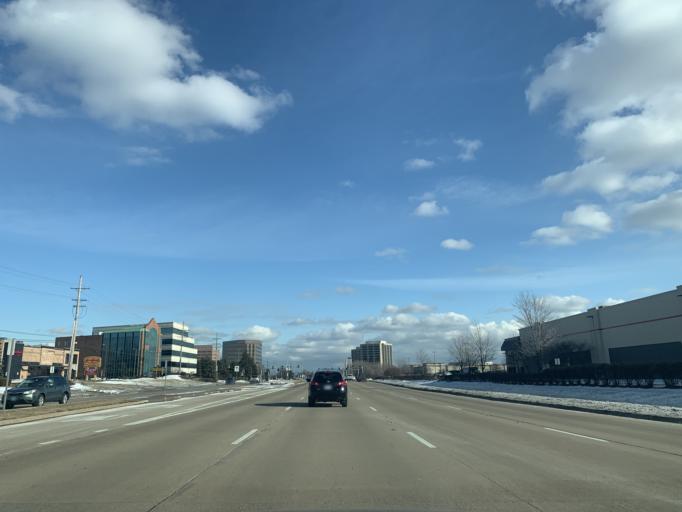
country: US
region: Illinois
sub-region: DuPage County
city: Oakbrook Terrace
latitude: 41.8463
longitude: -87.9664
